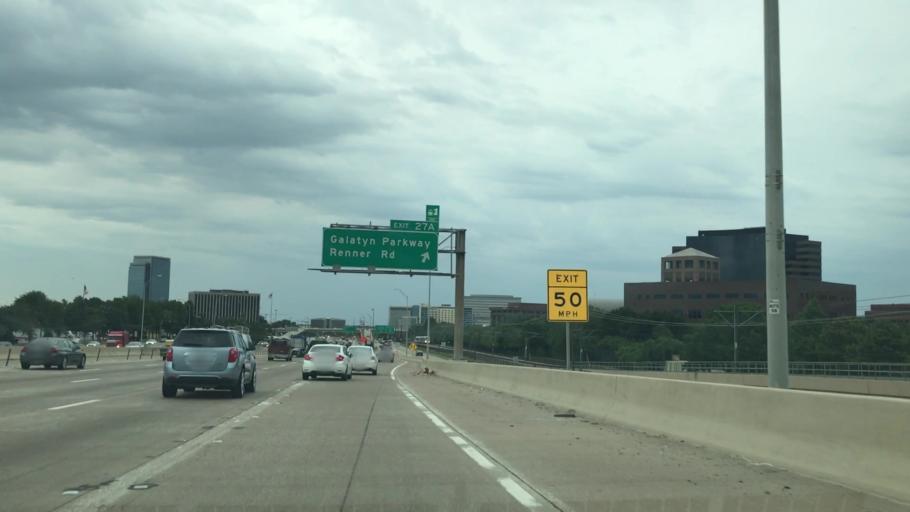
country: US
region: Texas
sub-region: Dallas County
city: Richardson
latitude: 32.9764
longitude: -96.7153
